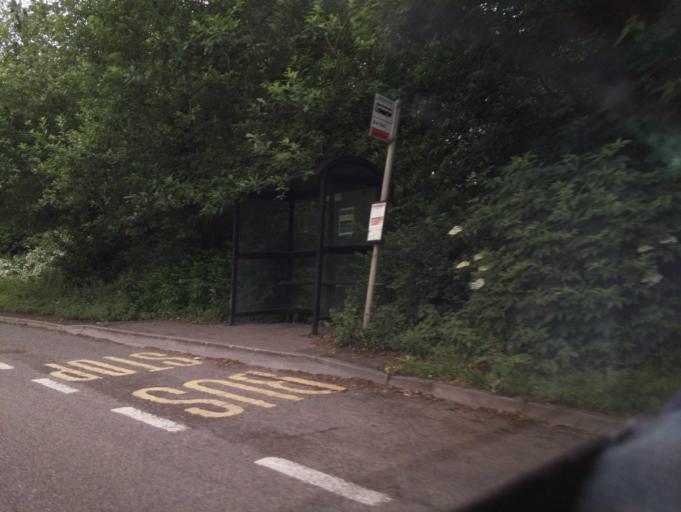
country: GB
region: England
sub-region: District of Rutland
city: Ridlington
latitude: 52.6020
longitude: -0.8748
